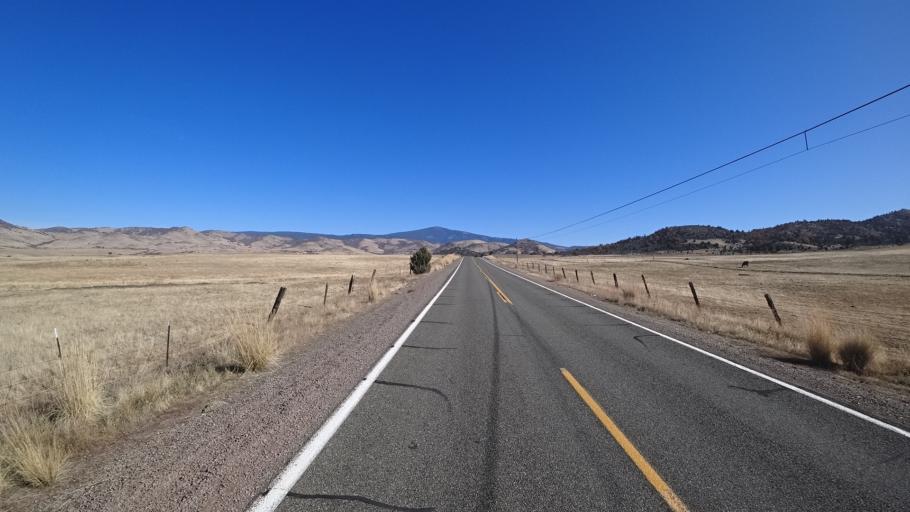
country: US
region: California
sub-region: Siskiyou County
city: Montague
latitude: 41.8044
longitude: -122.4051
